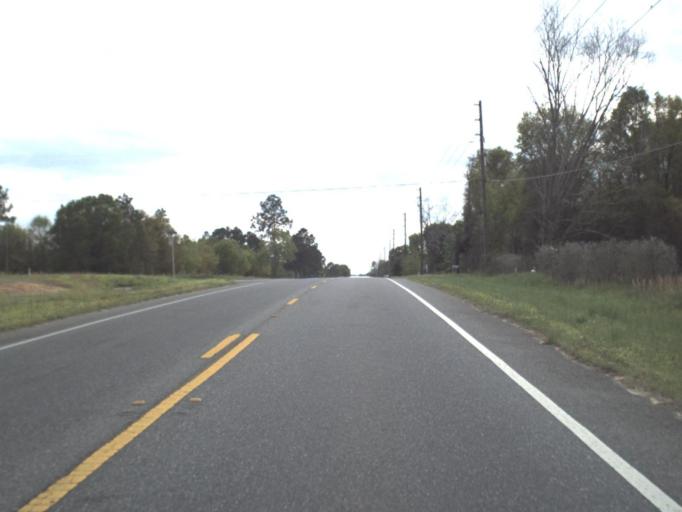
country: US
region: Florida
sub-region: Okaloosa County
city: Crestview
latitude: 30.8388
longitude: -86.5306
